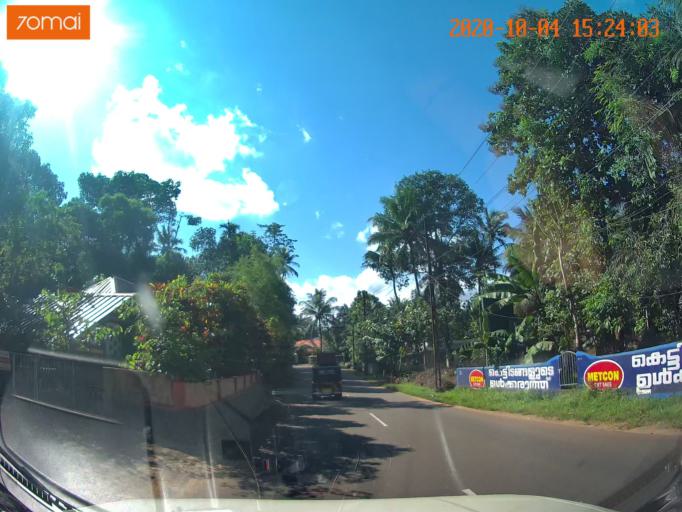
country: IN
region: Kerala
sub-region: Kottayam
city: Palackattumala
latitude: 9.7190
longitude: 76.6564
